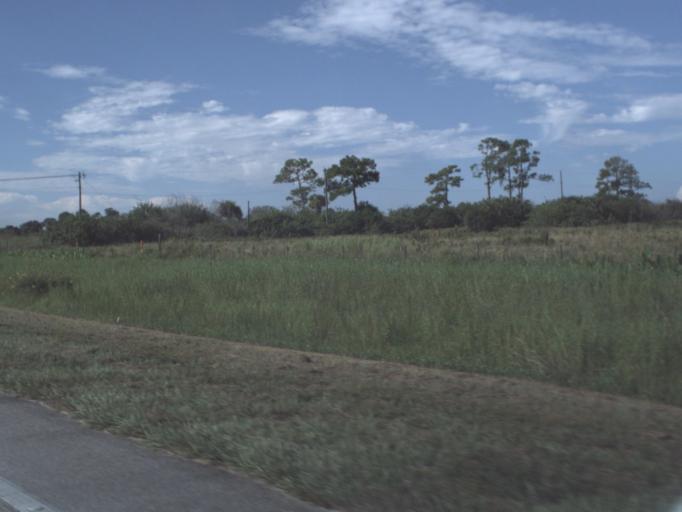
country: US
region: Florida
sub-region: Hendry County
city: Port LaBelle
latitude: 26.6472
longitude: -81.4361
